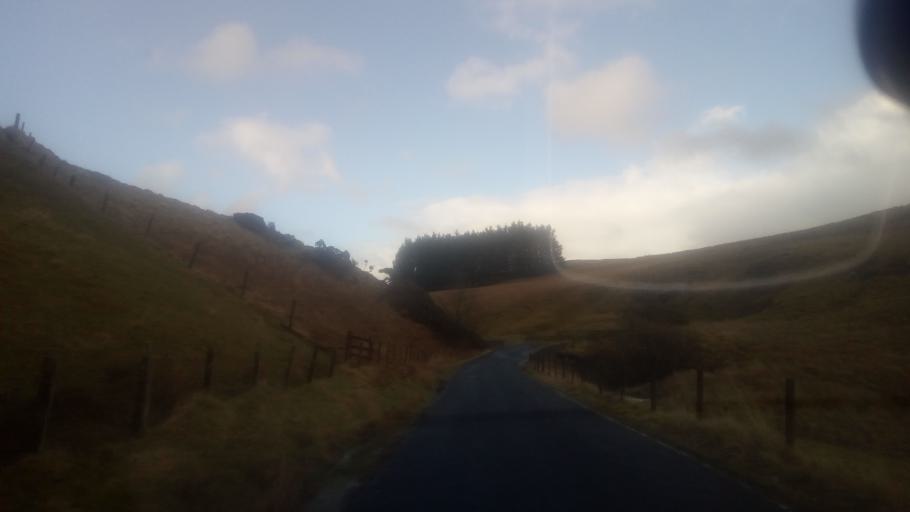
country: GB
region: Scotland
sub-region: The Scottish Borders
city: Innerleithen
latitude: 55.4550
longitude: -3.1089
